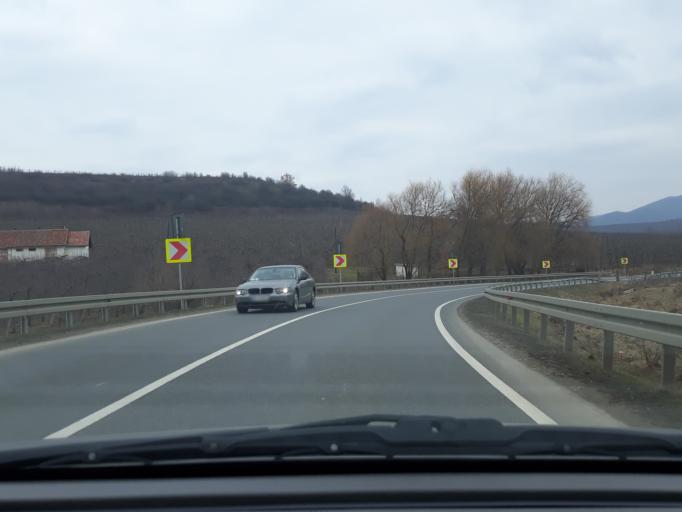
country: RO
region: Salaj
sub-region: Comuna Nusfalau
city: Nusfalau
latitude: 47.2217
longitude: 22.7483
